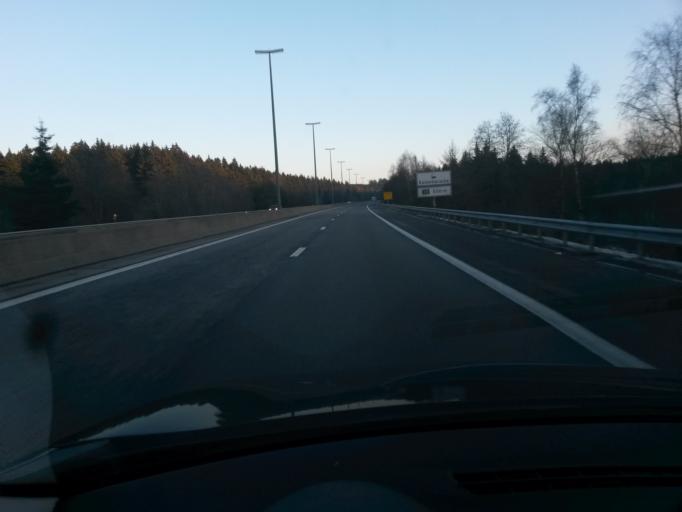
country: BE
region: Wallonia
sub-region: Province de Liege
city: Waimes
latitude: 50.3481
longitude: 6.0785
